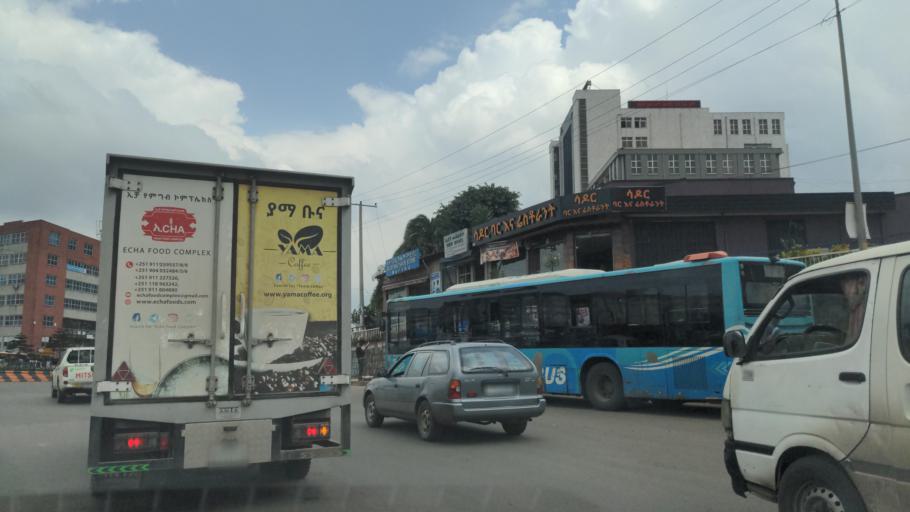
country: ET
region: Adis Abeba
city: Addis Ababa
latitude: 9.0218
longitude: 38.8015
